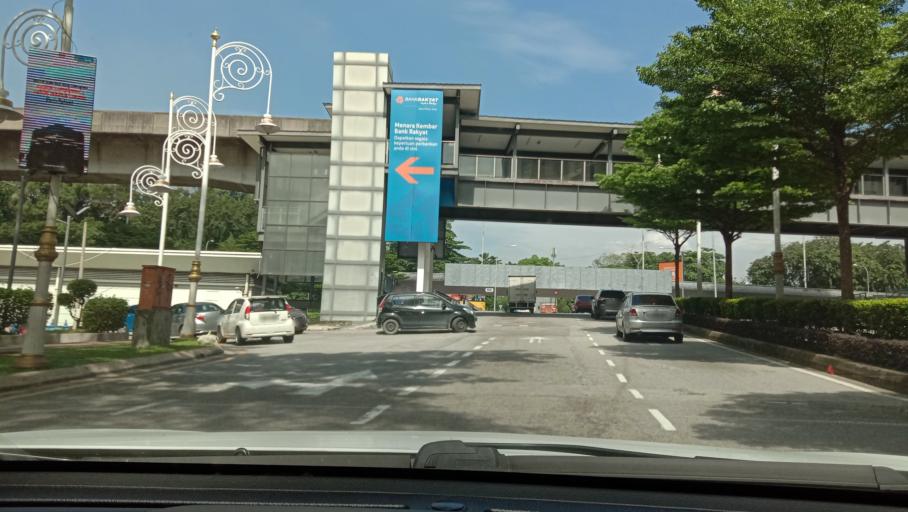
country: MY
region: Kuala Lumpur
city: Kuala Lumpur
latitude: 3.1310
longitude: 101.6833
